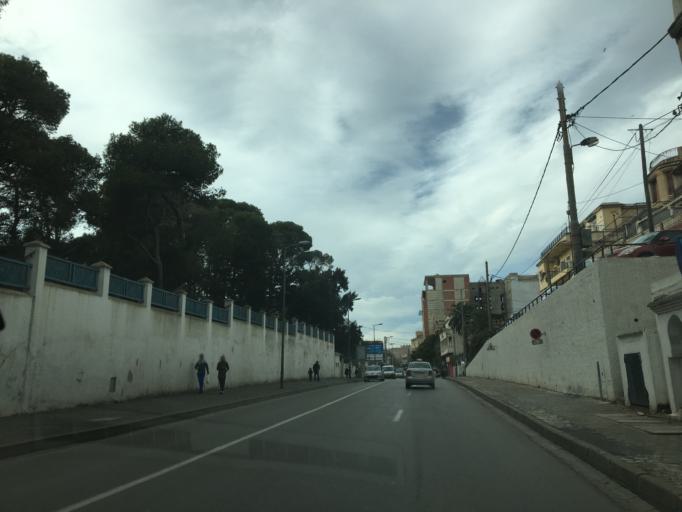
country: DZ
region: Alger
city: Algiers
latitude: 36.7711
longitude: 3.0395
